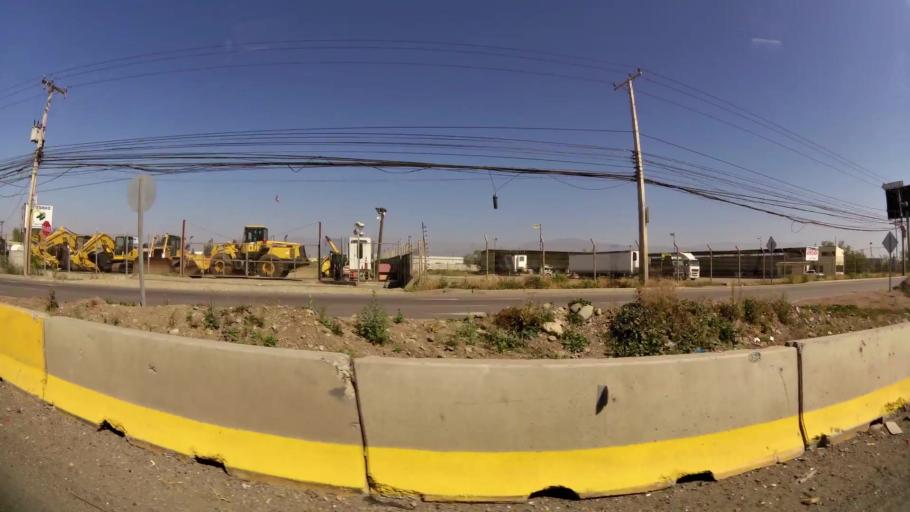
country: CL
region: Santiago Metropolitan
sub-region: Provincia de Chacabuco
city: Chicureo Abajo
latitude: -33.3107
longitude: -70.7256
